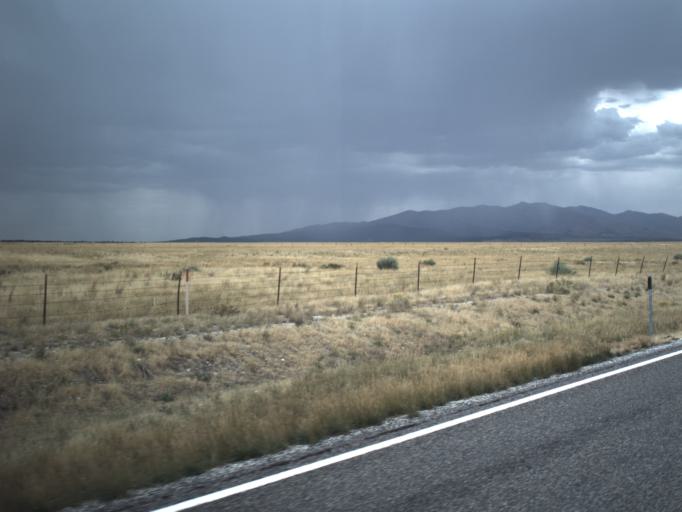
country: US
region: Idaho
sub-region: Oneida County
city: Malad City
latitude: 41.9034
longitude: -113.1048
